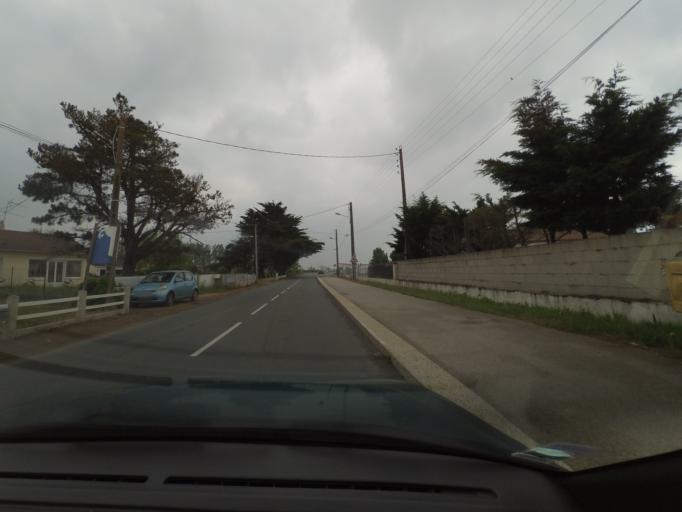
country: FR
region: Pays de la Loire
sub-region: Departement de la Vendee
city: Angles
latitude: 46.3437
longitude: -1.3451
